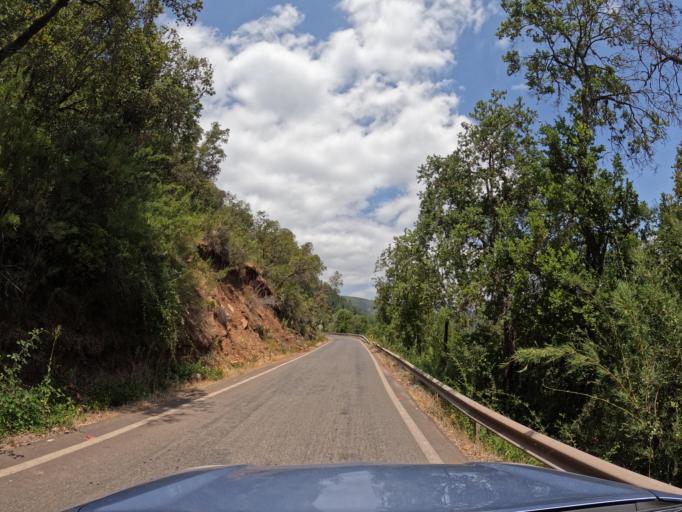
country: CL
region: Maule
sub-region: Provincia de Curico
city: Molina
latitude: -35.1764
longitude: -71.0874
